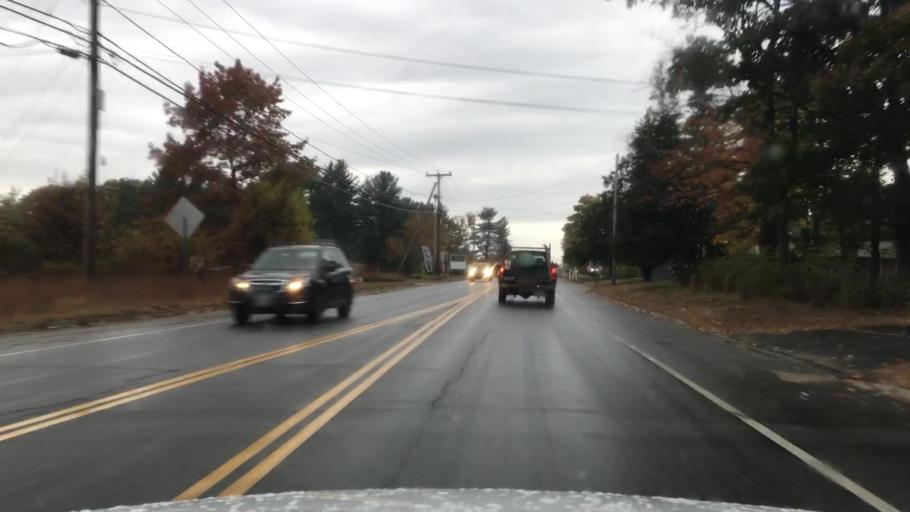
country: US
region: New Hampshire
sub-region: Strafford County
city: Somersworth
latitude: 43.2670
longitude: -70.9083
